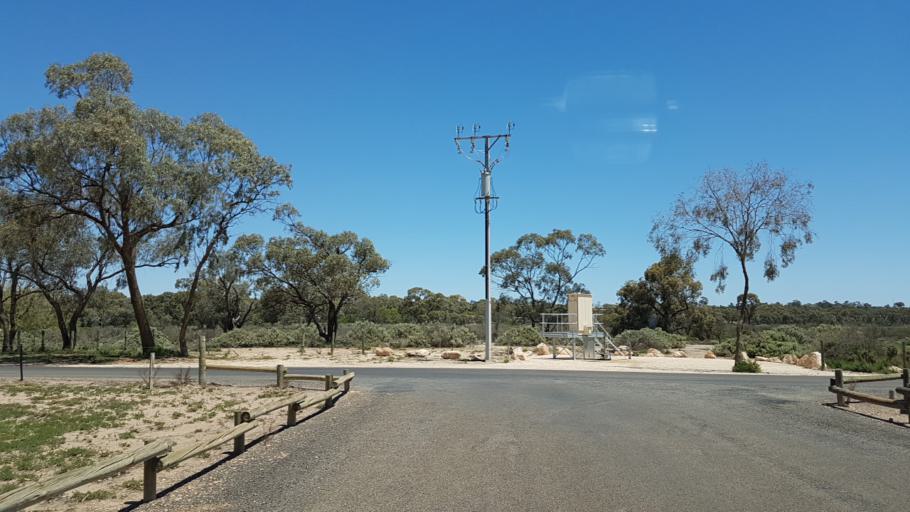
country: AU
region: South Australia
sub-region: Loxton Waikerie
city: Waikerie
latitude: -34.1721
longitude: 139.9804
